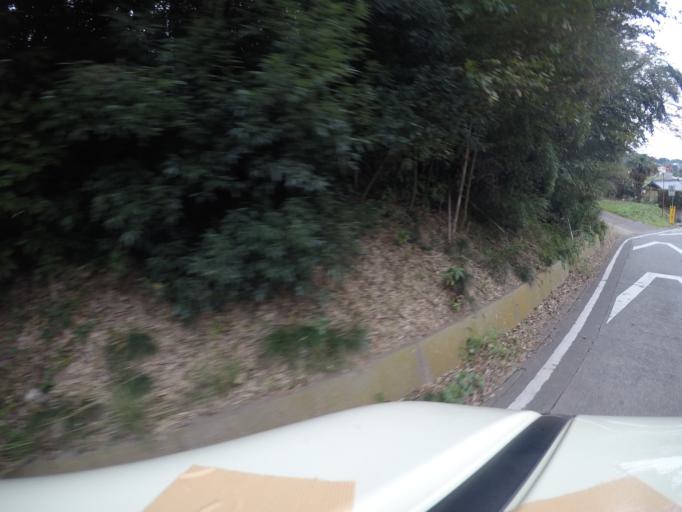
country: JP
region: Ibaraki
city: Naka
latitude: 36.0646
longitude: 140.1626
